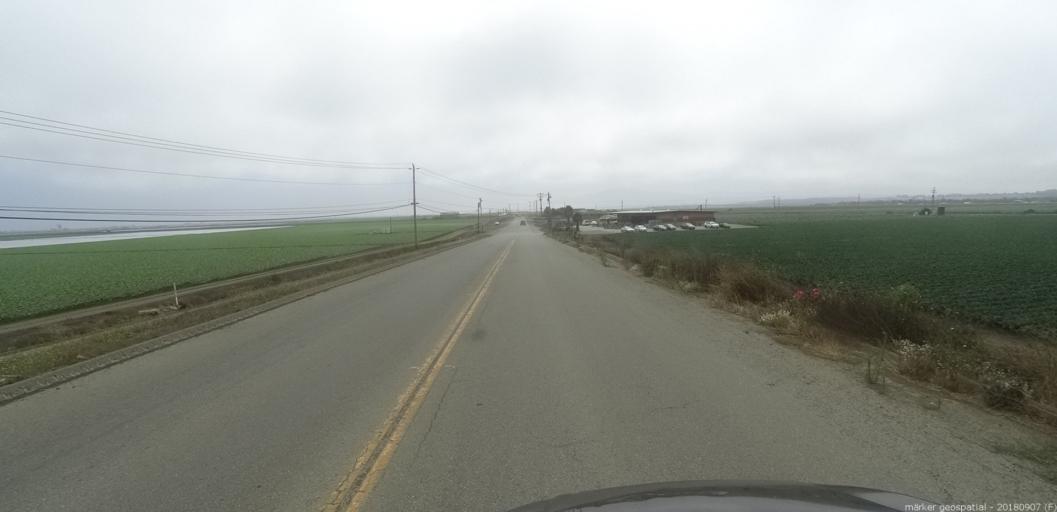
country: US
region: California
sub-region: Monterey County
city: Castroville
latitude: 36.7442
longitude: -121.7696
